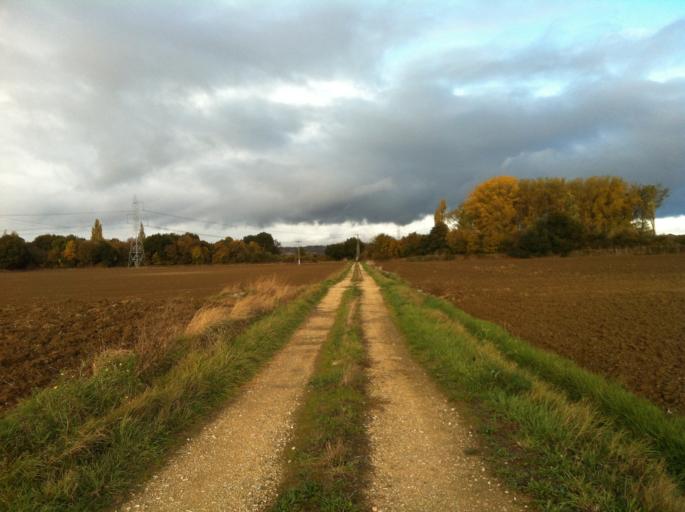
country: ES
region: Basque Country
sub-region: Provincia de Alava
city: Gasteiz / Vitoria
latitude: 42.8622
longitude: -2.7227
